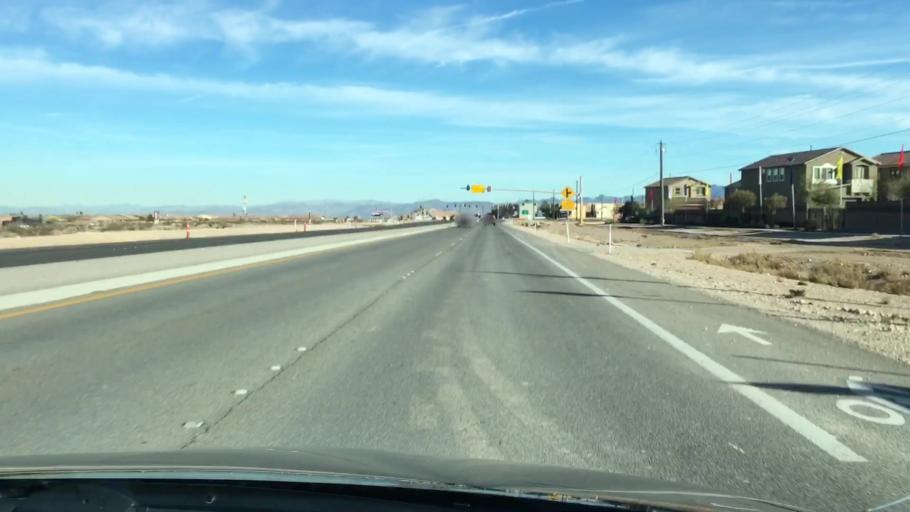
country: US
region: Nevada
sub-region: Clark County
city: Enterprise
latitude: 36.0210
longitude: -115.3024
